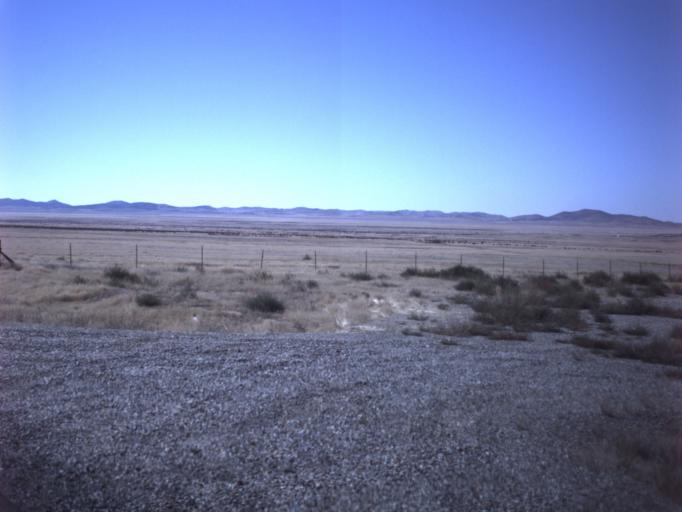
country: US
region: Utah
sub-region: Tooele County
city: Grantsville
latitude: 40.3831
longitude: -112.7470
